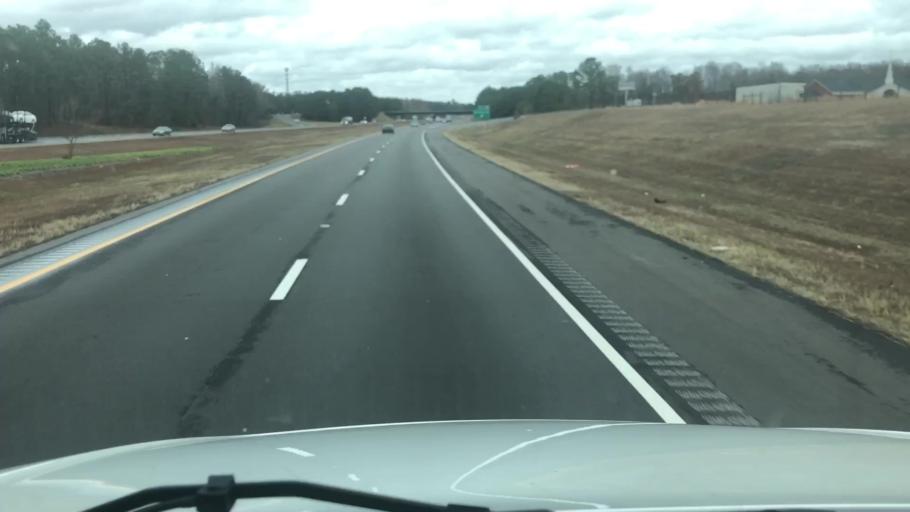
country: US
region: North Carolina
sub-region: Cumberland County
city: Eastover
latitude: 35.0772
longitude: -78.7893
